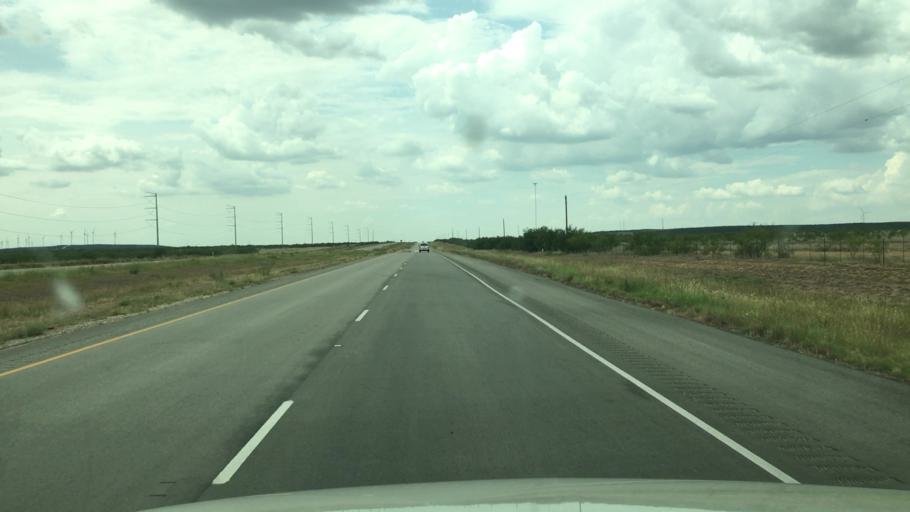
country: US
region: Texas
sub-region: Glasscock County
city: Garden City
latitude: 31.9717
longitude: -101.2430
